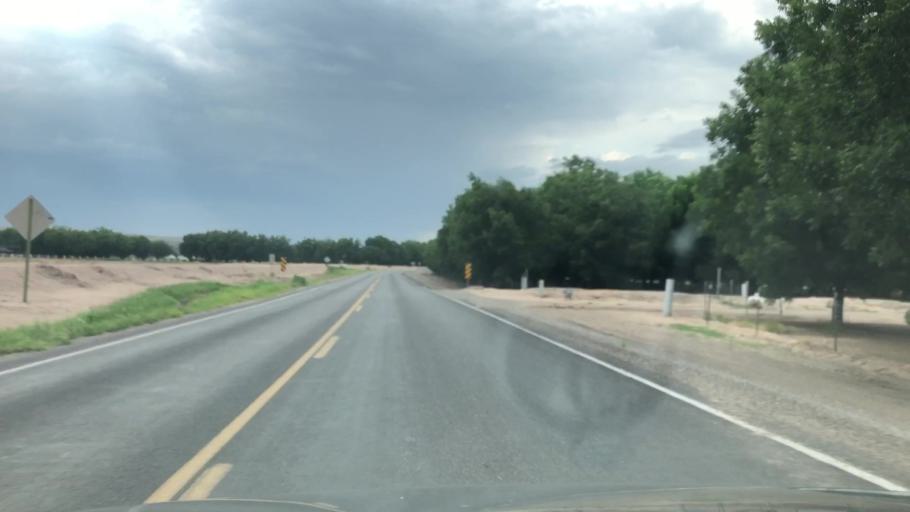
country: US
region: New Mexico
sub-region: Dona Ana County
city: Anthony
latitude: 32.0031
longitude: -106.6581
